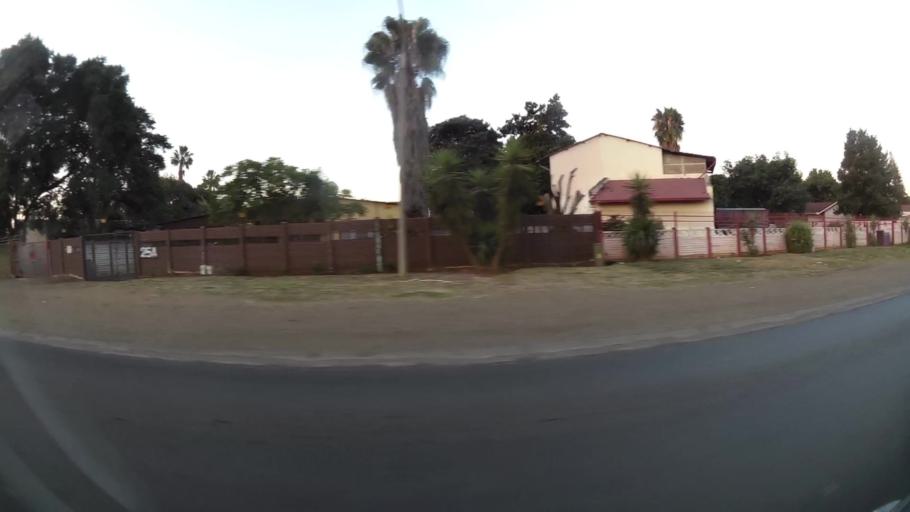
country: ZA
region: North-West
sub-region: Bojanala Platinum District Municipality
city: Rustenburg
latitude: -25.6601
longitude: 27.2477
